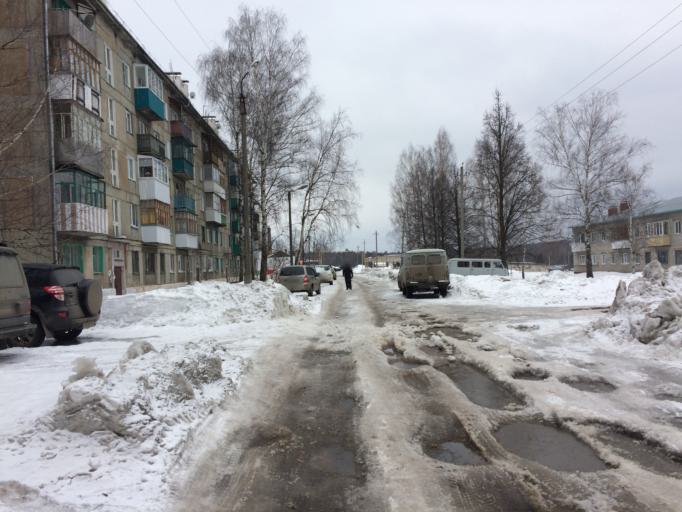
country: RU
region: Mariy-El
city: Mochalishche
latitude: 56.5449
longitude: 48.4024
